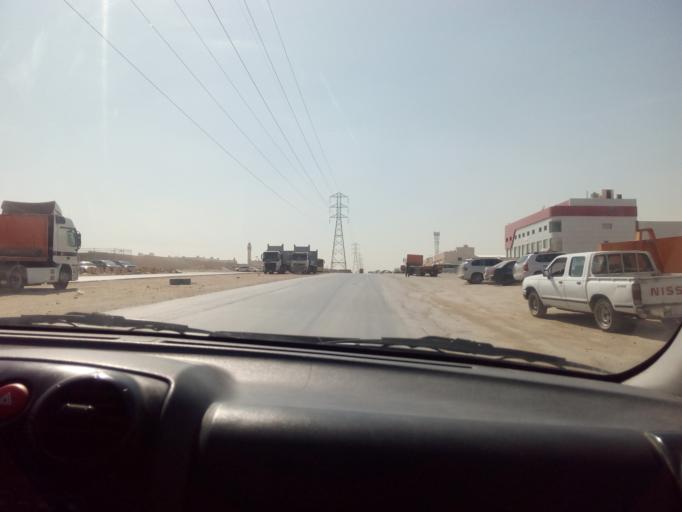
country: SA
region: Ar Riyad
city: Riyadh
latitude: 24.6644
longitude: 46.8414
